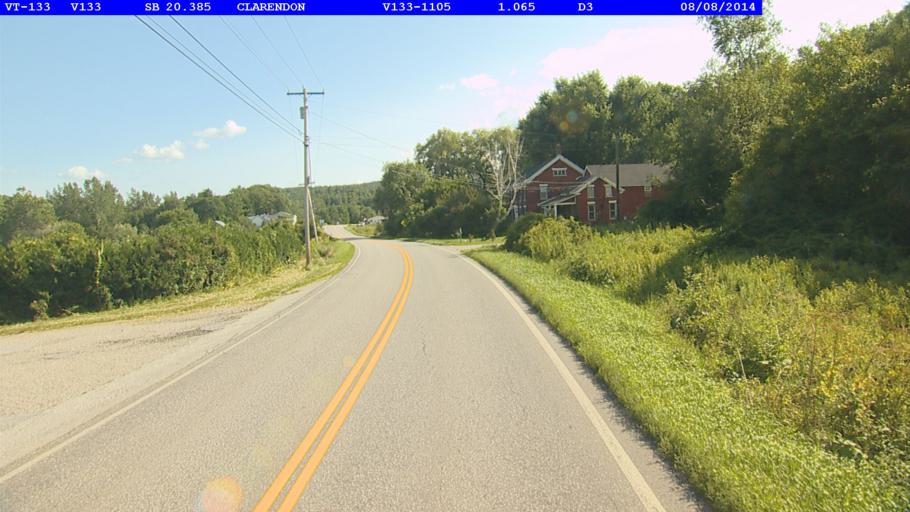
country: US
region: Vermont
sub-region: Rutland County
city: West Rutland
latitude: 43.5655
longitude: -73.0330
